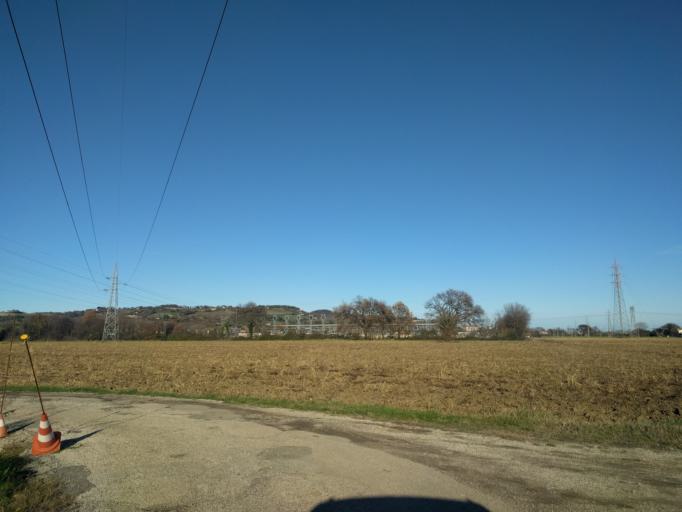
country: IT
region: The Marches
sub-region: Provincia di Pesaro e Urbino
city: Cuccurano
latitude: 43.7831
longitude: 12.9526
